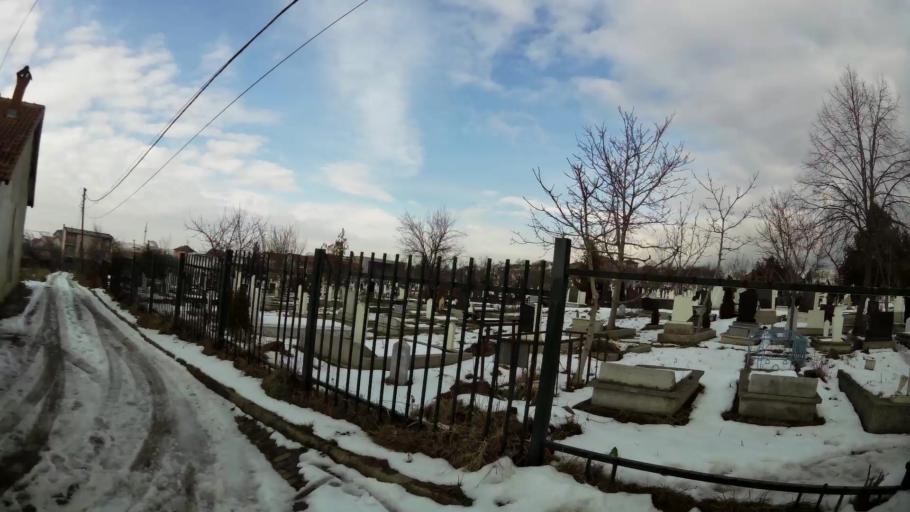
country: XK
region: Pristina
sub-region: Komuna e Prishtines
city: Pristina
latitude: 42.6714
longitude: 21.1518
